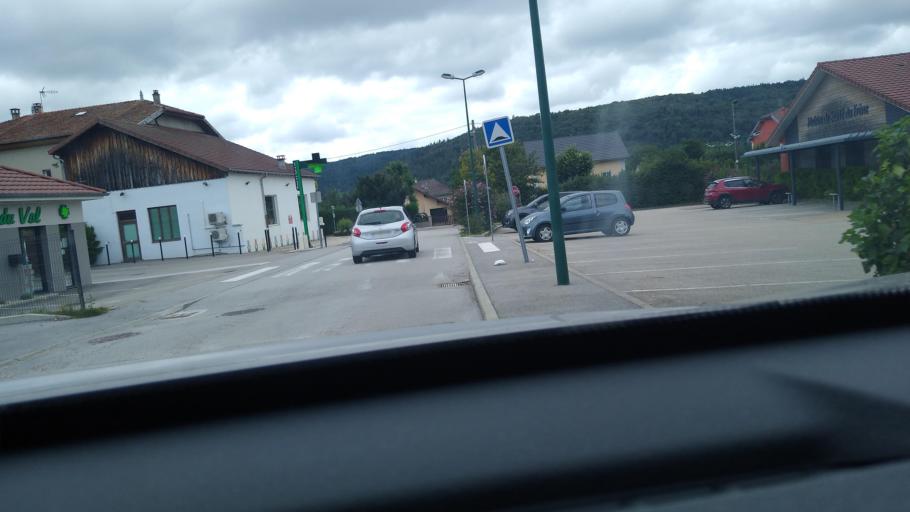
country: FR
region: Rhone-Alpes
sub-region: Departement de l'Ain
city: Saint-Martin-du-Frene
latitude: 46.1361
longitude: 5.5521
